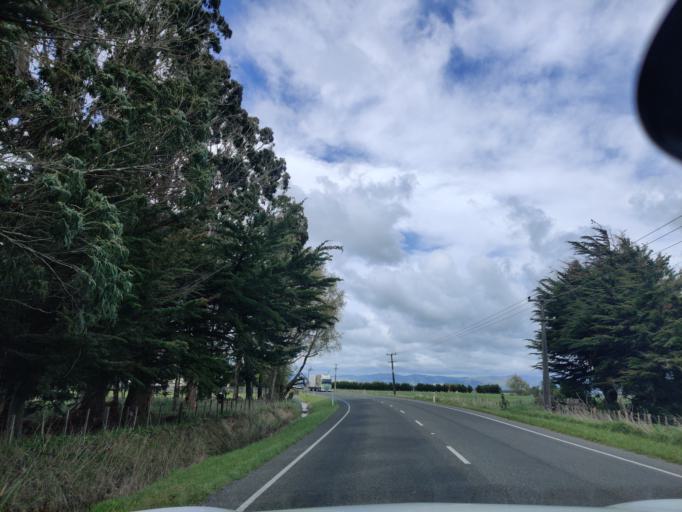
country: NZ
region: Manawatu-Wanganui
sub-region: Palmerston North City
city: Palmerston North
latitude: -40.3275
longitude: 175.5071
